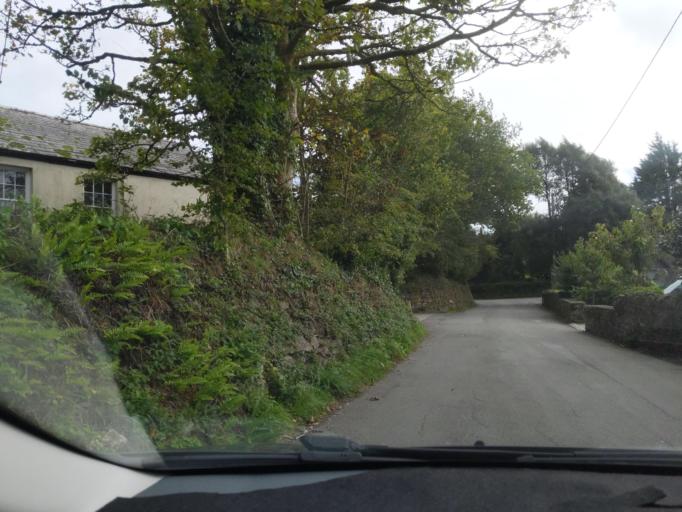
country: GB
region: England
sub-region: Cornwall
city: Lostwithiel
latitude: 50.3996
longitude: -4.7035
